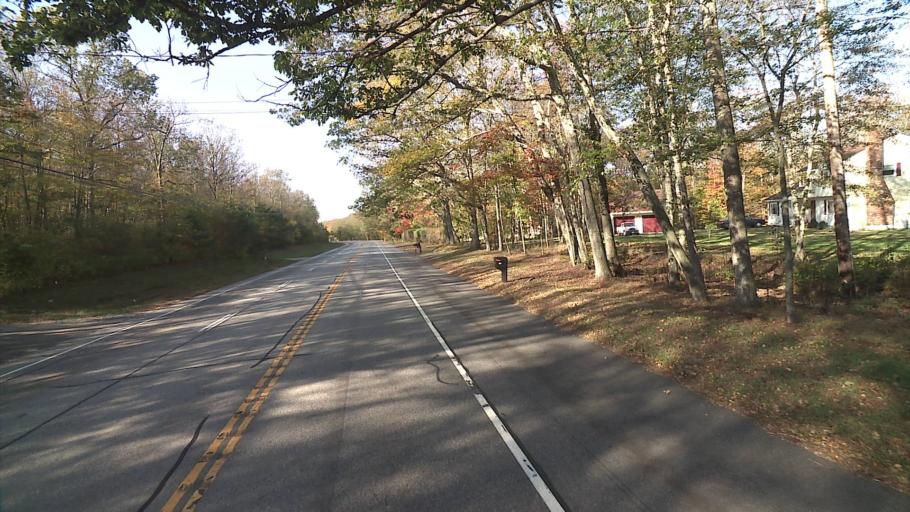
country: US
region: Connecticut
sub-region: Windham County
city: Wauregan
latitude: 41.7790
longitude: -72.0300
